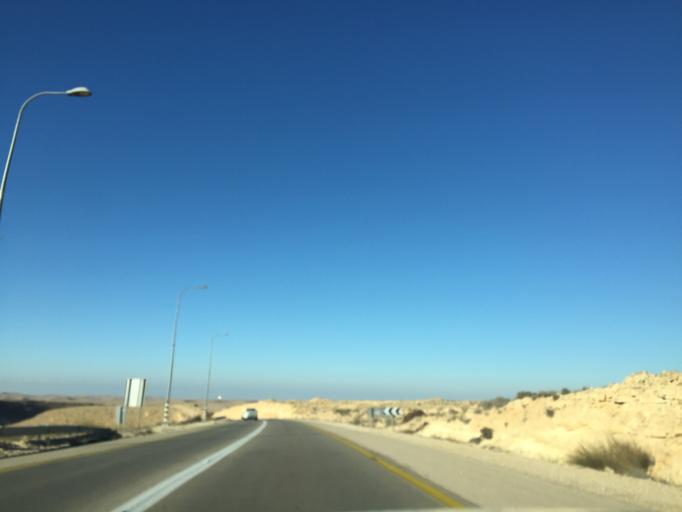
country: IL
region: Southern District
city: Midreshet Ben-Gurion
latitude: 30.7386
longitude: 34.7696
